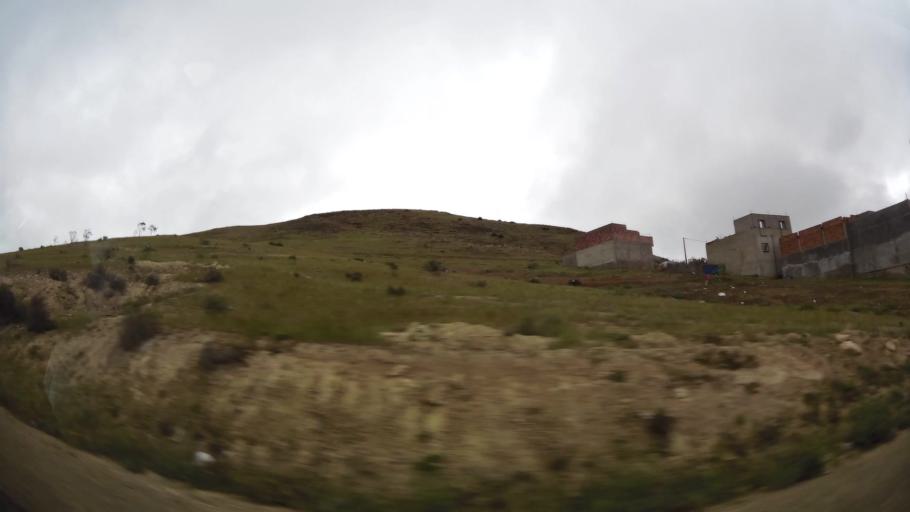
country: MA
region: Oriental
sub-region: Nador
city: Midar
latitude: 35.0657
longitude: -3.4700
